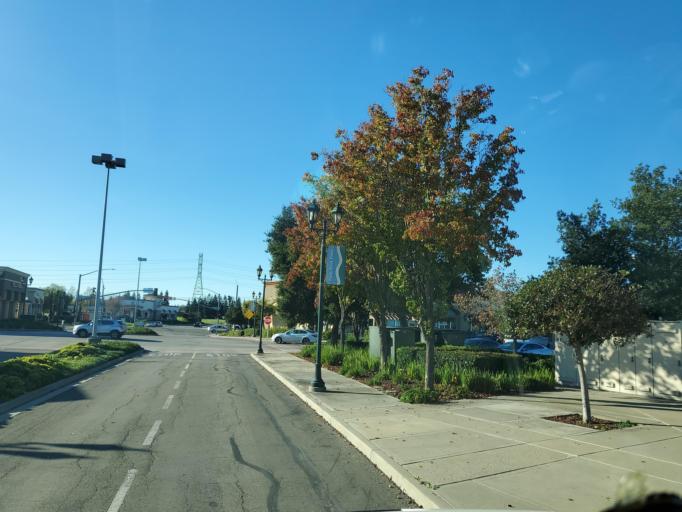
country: US
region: California
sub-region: San Joaquin County
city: Lincoln Village
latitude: 38.0537
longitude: -121.3739
